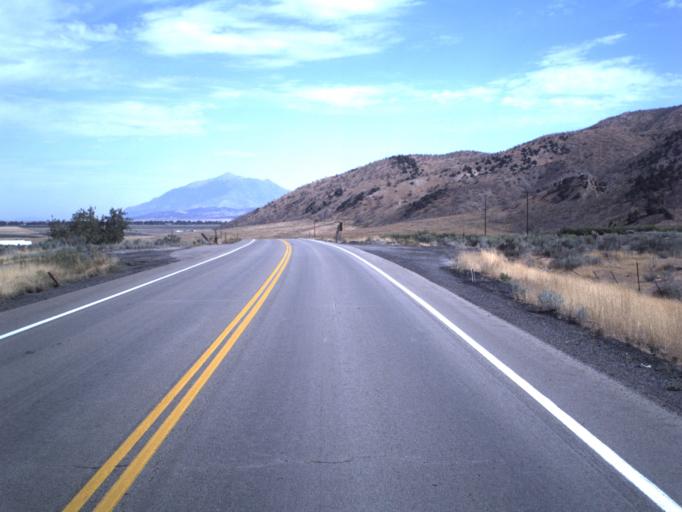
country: US
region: Utah
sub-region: Juab County
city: Nephi
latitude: 39.5105
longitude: -111.8694
